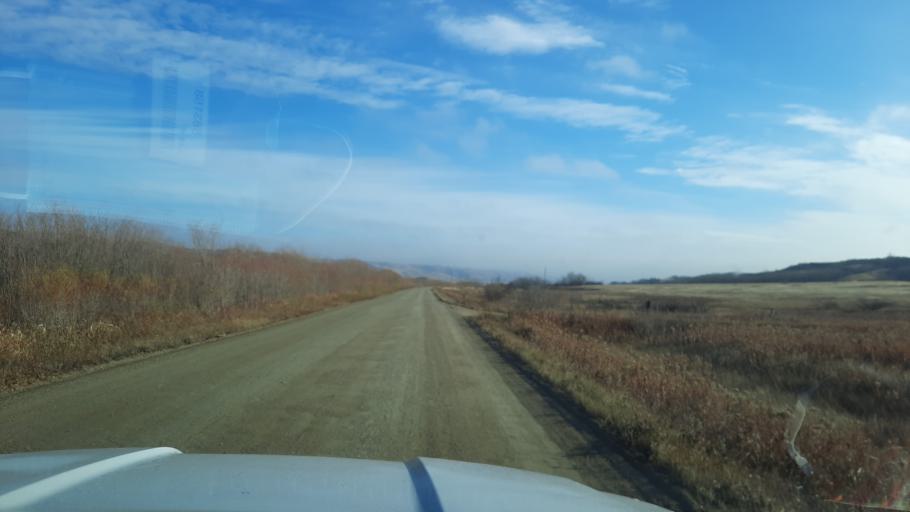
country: CA
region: Saskatchewan
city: Pilot Butte
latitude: 50.7816
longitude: -104.2683
